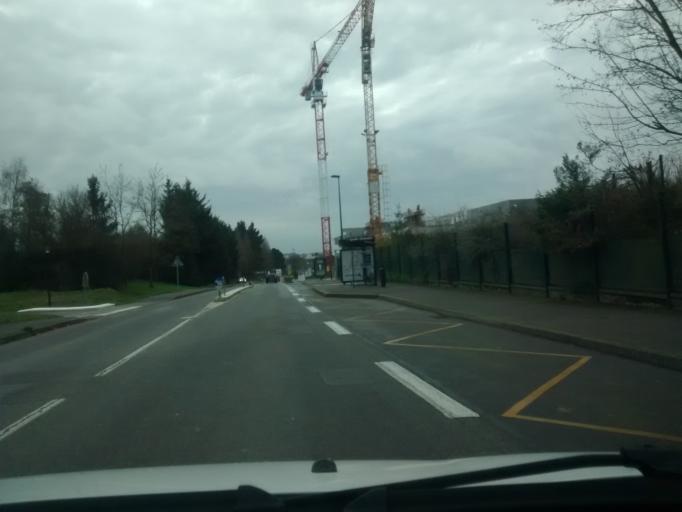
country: FR
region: Brittany
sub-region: Departement d'Ille-et-Vilaine
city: Cesson-Sevigne
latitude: 48.1312
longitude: -1.5969
